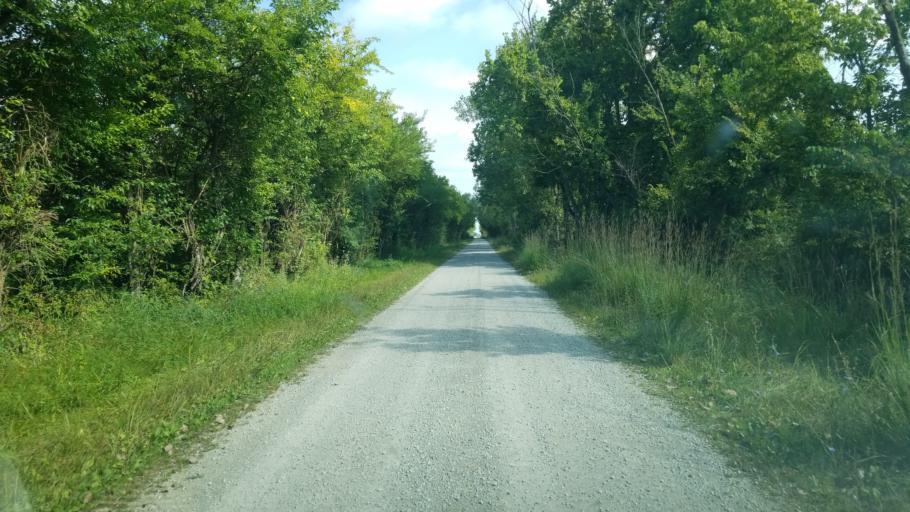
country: US
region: Ohio
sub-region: Wyandot County
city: Upper Sandusky
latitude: 40.6994
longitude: -83.3239
